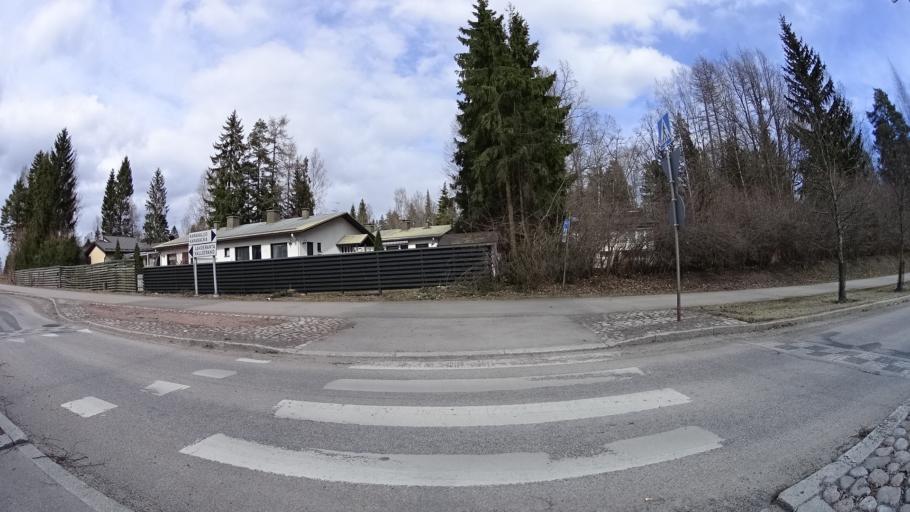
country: FI
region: Uusimaa
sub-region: Helsinki
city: Kauniainen
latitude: 60.2345
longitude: 24.7450
